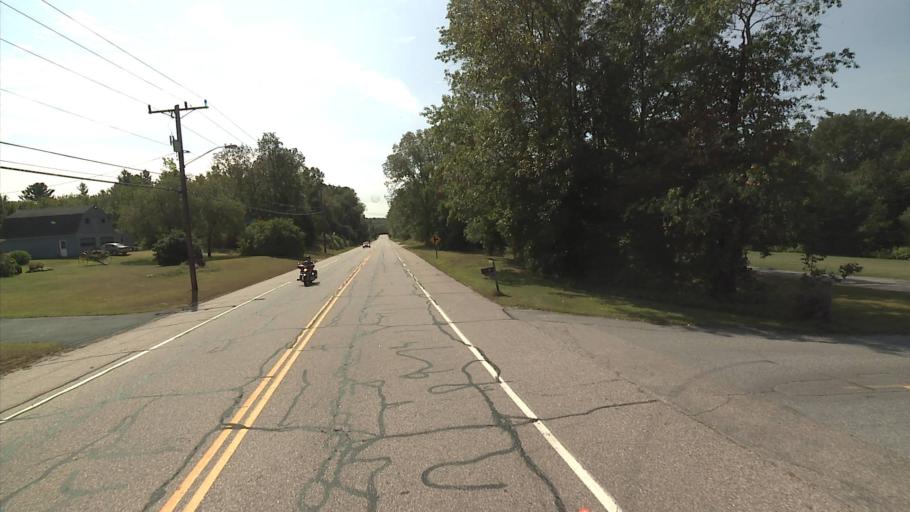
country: US
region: Connecticut
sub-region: New London County
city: Lisbon
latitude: 41.6011
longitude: -72.0178
